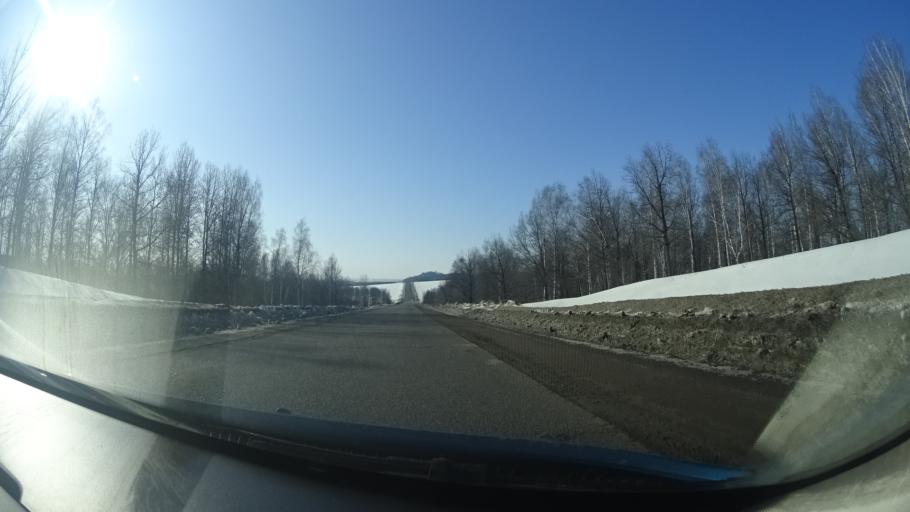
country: RU
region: Bashkortostan
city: Starobaltachevo
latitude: 56.1004
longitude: 55.9407
